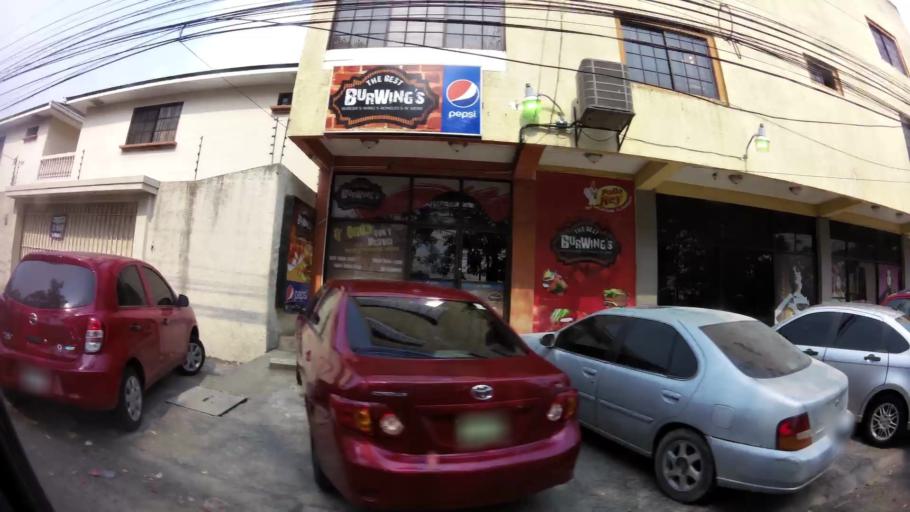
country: HN
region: Cortes
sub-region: San Pedro Sula
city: Pena Blanca
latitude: 15.5297
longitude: -88.0276
